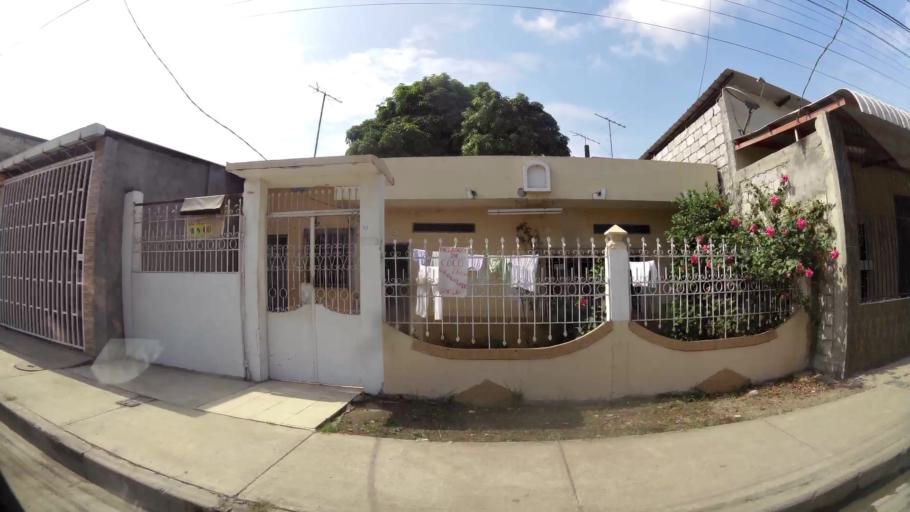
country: EC
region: Guayas
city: Guayaquil
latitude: -2.2772
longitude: -79.8785
